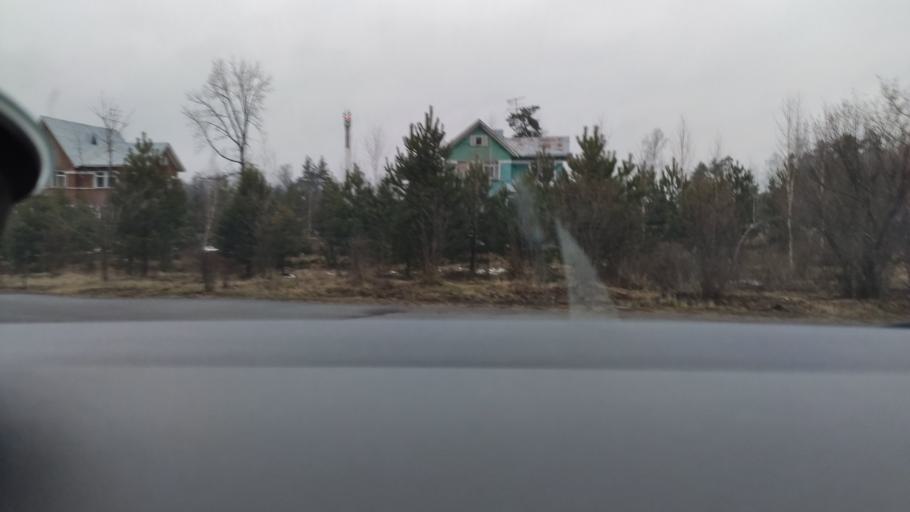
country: RU
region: Moskovskaya
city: Zhavoronki
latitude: 55.7035
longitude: 37.0985
